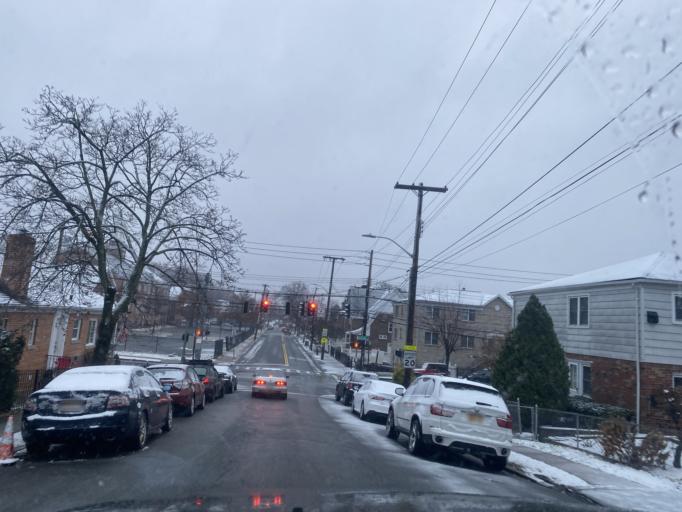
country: US
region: New York
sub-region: Westchester County
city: Mount Vernon
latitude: 40.9067
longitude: -73.8636
